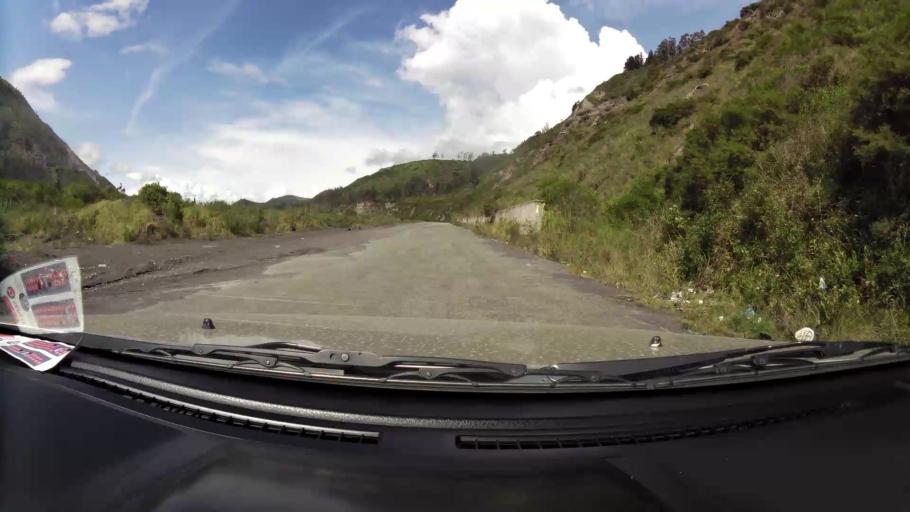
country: EC
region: Tungurahua
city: Banos
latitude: -1.5013
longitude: -78.5166
